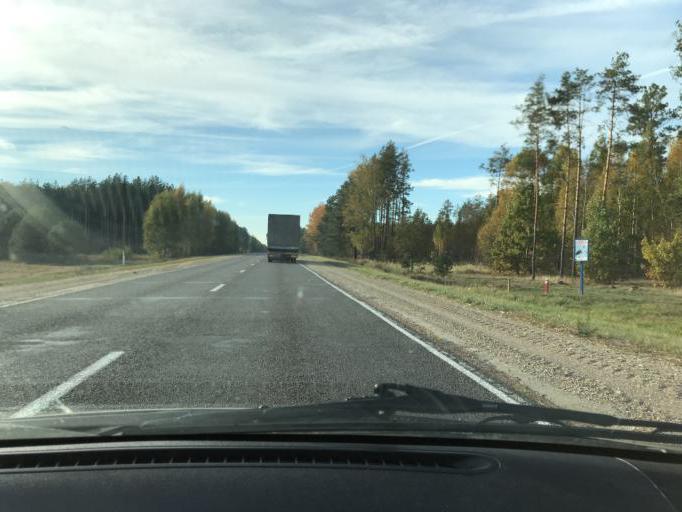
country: BY
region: Brest
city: Horad Pinsk
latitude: 52.1506
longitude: 25.8549
